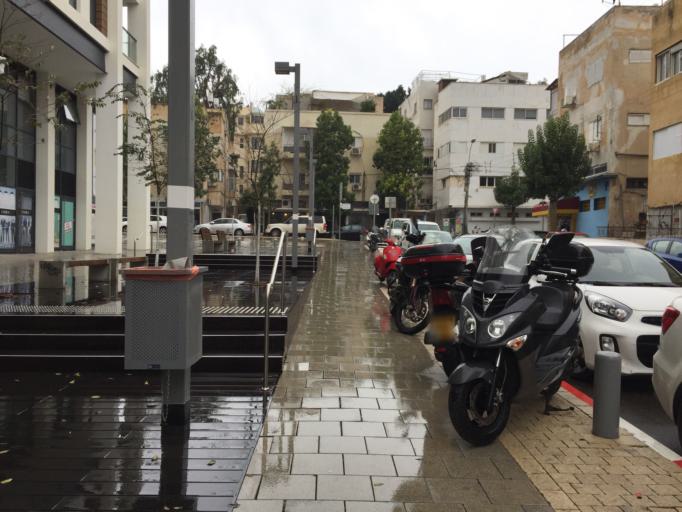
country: IL
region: Tel Aviv
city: Tel Aviv
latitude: 32.0715
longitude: 34.7716
